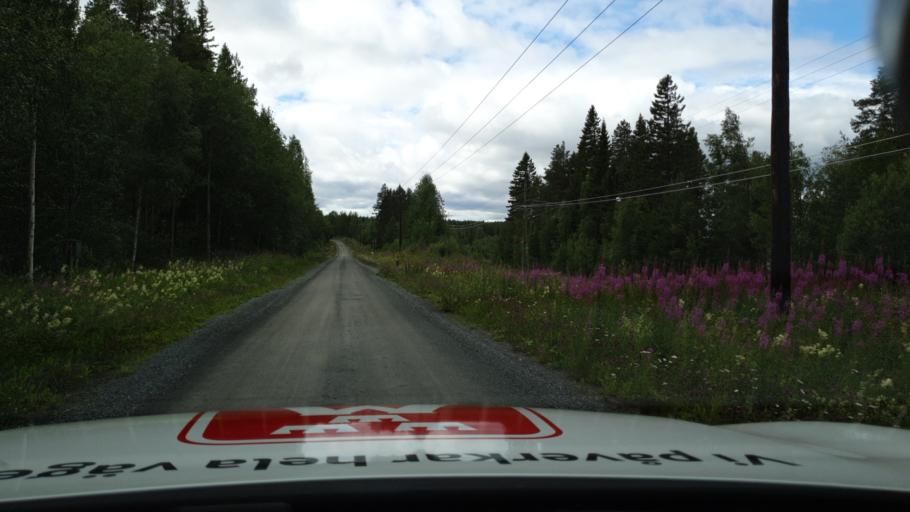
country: SE
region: Jaemtland
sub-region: Krokoms Kommun
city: Krokom
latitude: 63.3500
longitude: 14.3119
